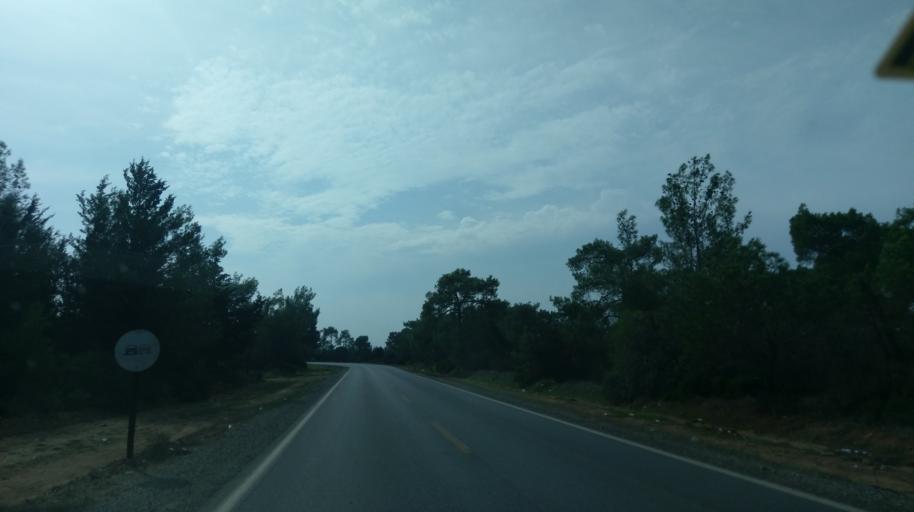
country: CY
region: Lefkosia
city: Morfou
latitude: 35.2905
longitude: 33.0413
